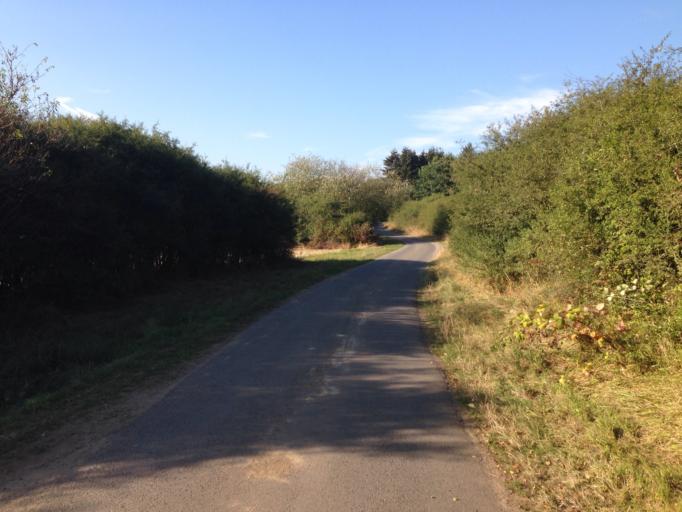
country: DE
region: Hesse
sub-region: Regierungsbezirk Giessen
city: Grossen Buseck
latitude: 50.5533
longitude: 8.7511
